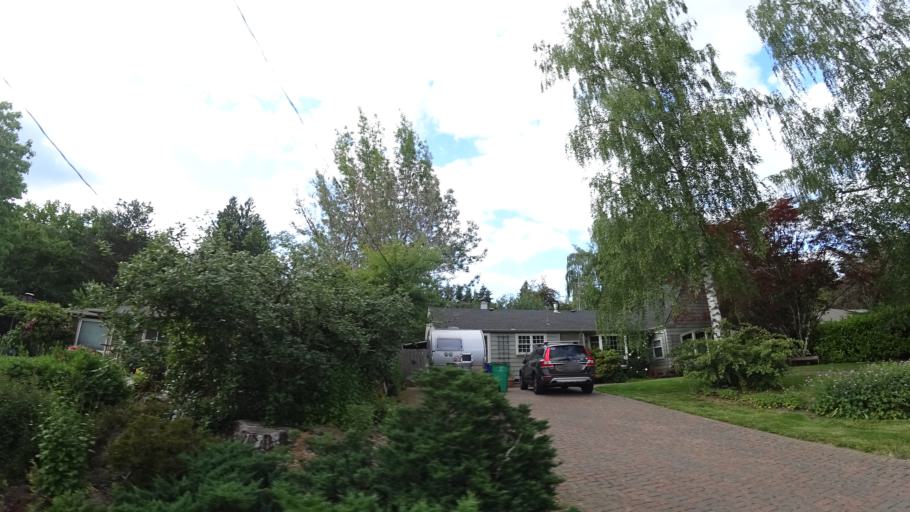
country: US
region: Oregon
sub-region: Washington County
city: Garden Home-Whitford
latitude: 45.4773
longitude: -122.7309
